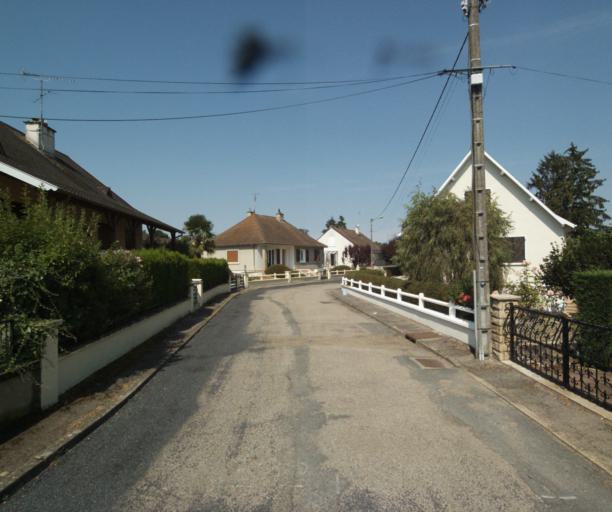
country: FR
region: Bourgogne
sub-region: Departement de Saone-et-Loire
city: Gueugnon
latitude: 46.5976
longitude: 4.0624
